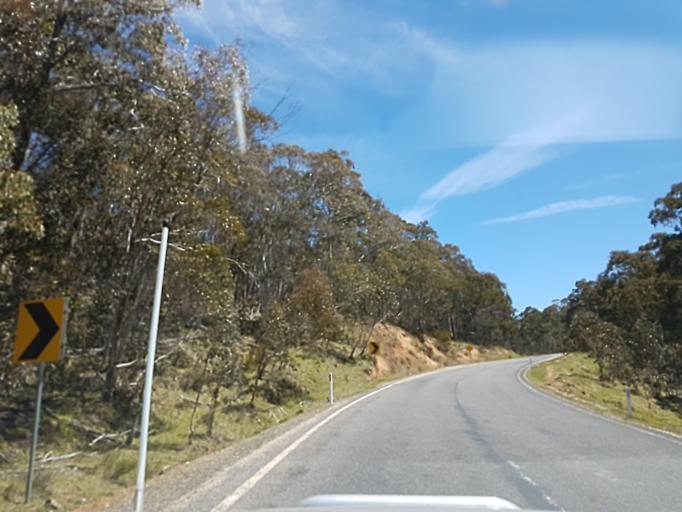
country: AU
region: Victoria
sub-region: Alpine
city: Mount Beauty
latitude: -37.0827
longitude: 147.3749
